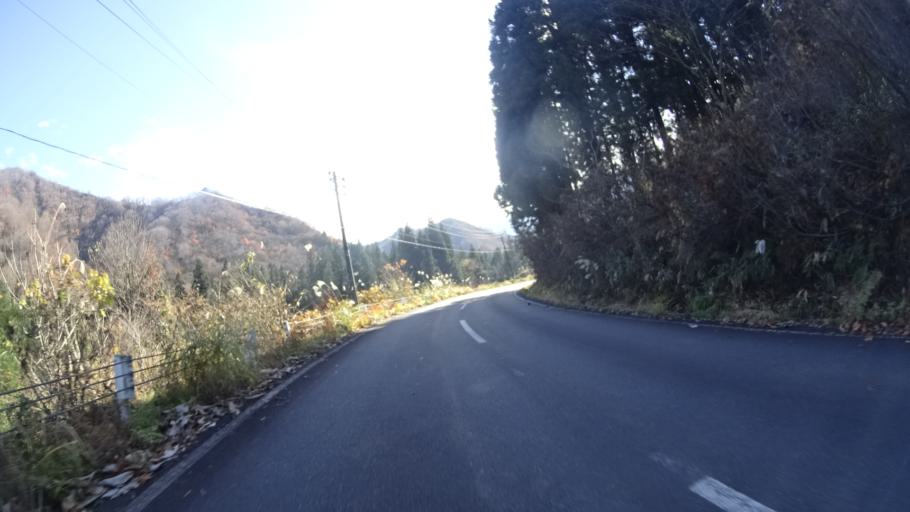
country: JP
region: Niigata
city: Muikamachi
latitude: 37.1896
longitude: 139.0817
